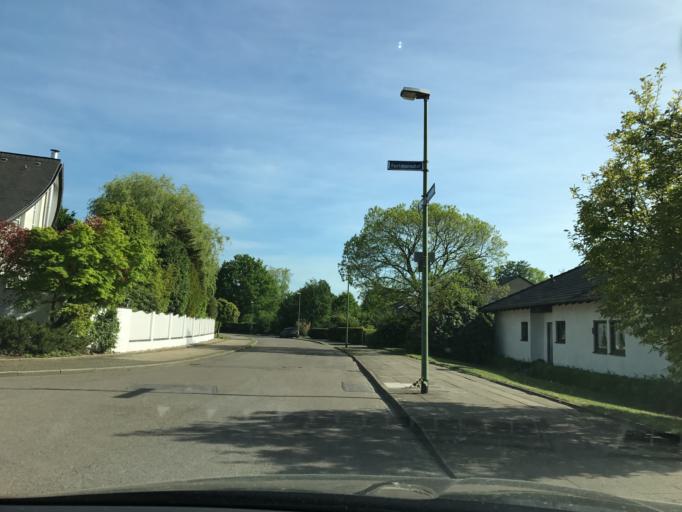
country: DE
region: North Rhine-Westphalia
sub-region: Regierungsbezirk Dusseldorf
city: Essen
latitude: 51.4017
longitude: 6.9798
